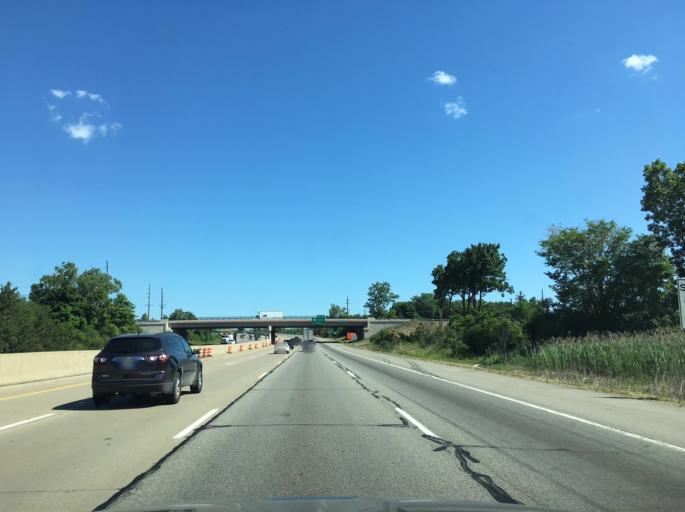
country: US
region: Michigan
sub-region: Oakland County
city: Auburn Hills
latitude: 42.6767
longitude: -83.2411
